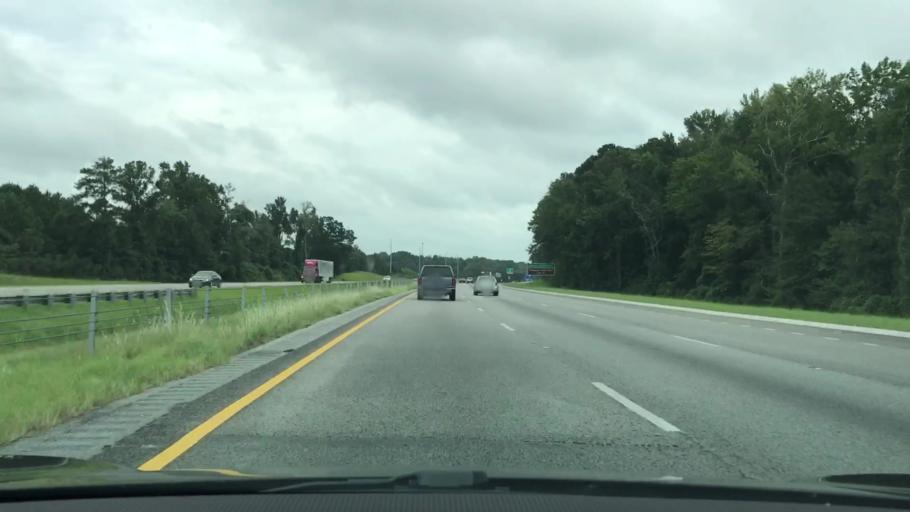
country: US
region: Alabama
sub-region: Lee County
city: Auburn
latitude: 32.5509
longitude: -85.5233
